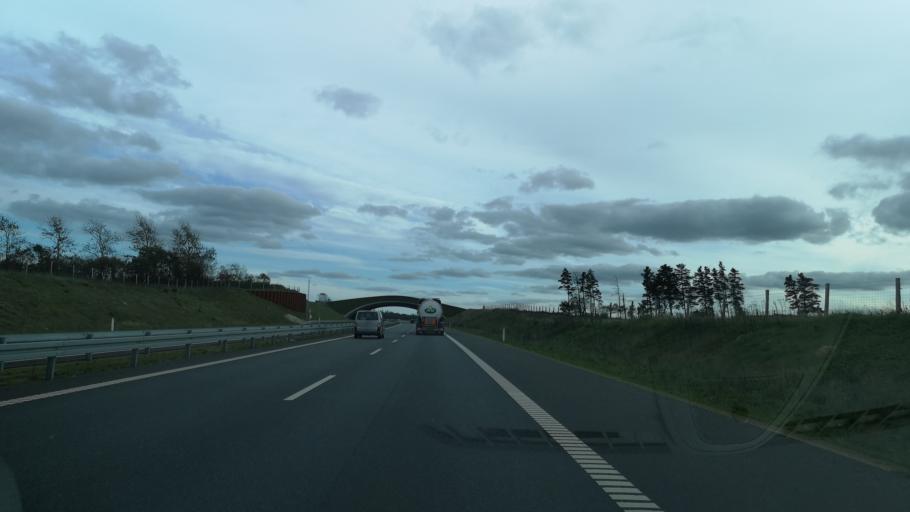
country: DK
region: Central Jutland
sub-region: Herning Kommune
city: Avlum
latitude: 56.2813
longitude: 8.7378
